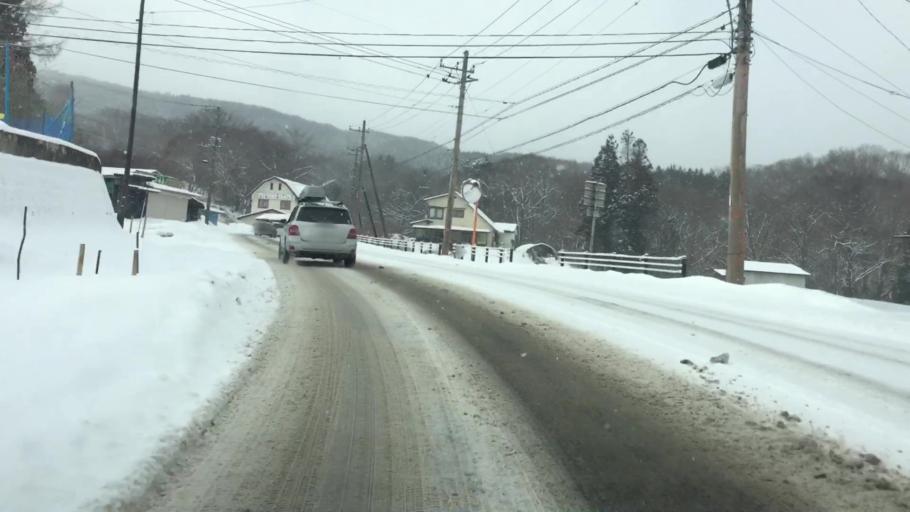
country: JP
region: Tochigi
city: Yaita
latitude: 36.9546
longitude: 139.7734
